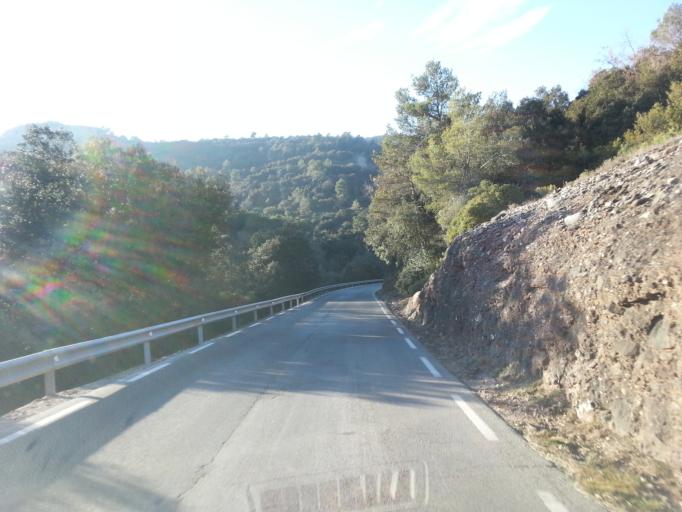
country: ES
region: Catalonia
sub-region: Provincia de Barcelona
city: Mura
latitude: 41.6528
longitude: 1.9799
